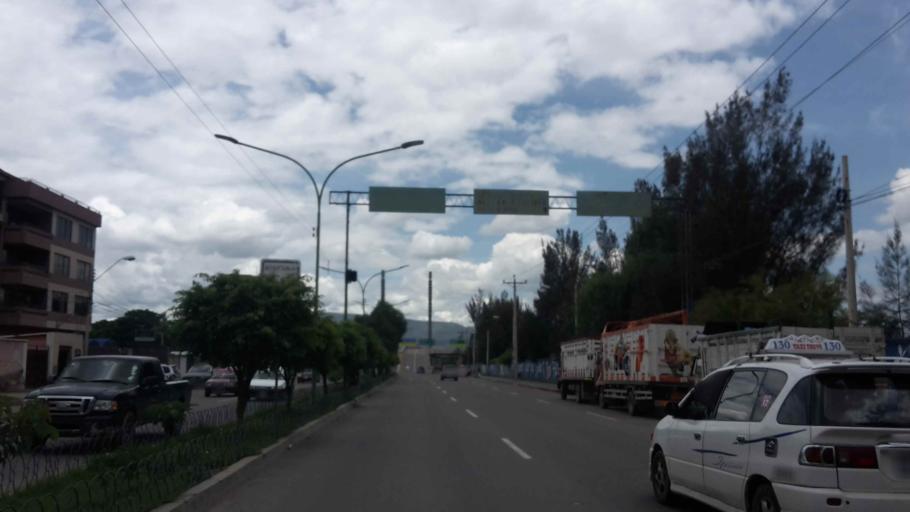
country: BO
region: Cochabamba
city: Cochabamba
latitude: -17.3908
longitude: -66.1795
